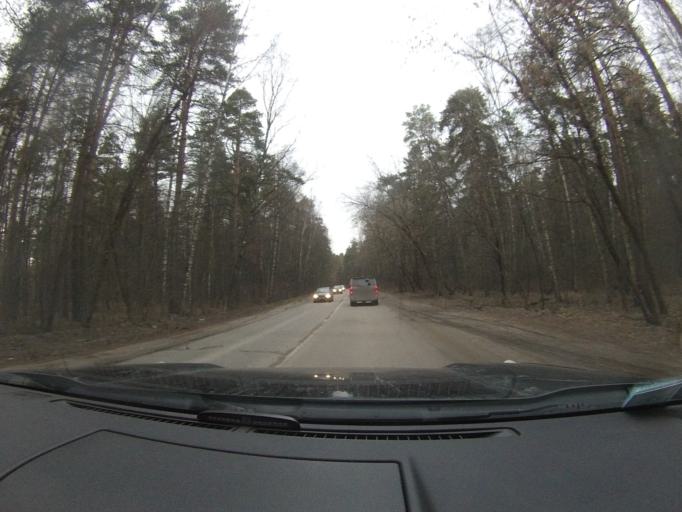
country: RU
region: Moskovskaya
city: Voskresensk
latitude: 55.3353
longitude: 38.6753
